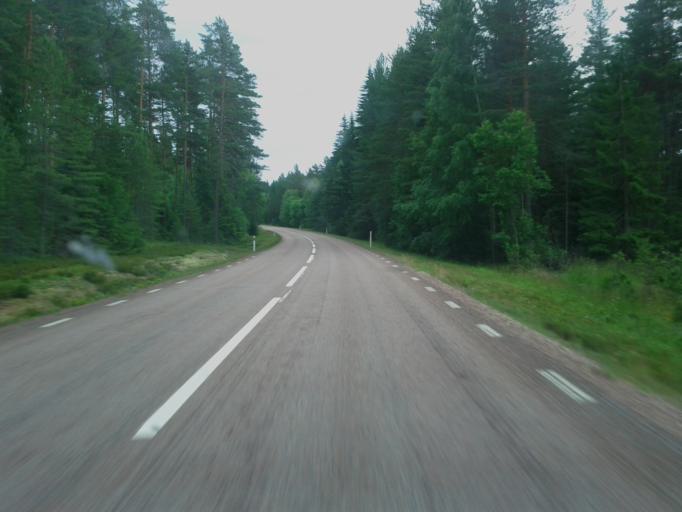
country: SE
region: Dalarna
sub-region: Mora Kommun
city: Mora
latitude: 61.0903
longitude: 14.3062
